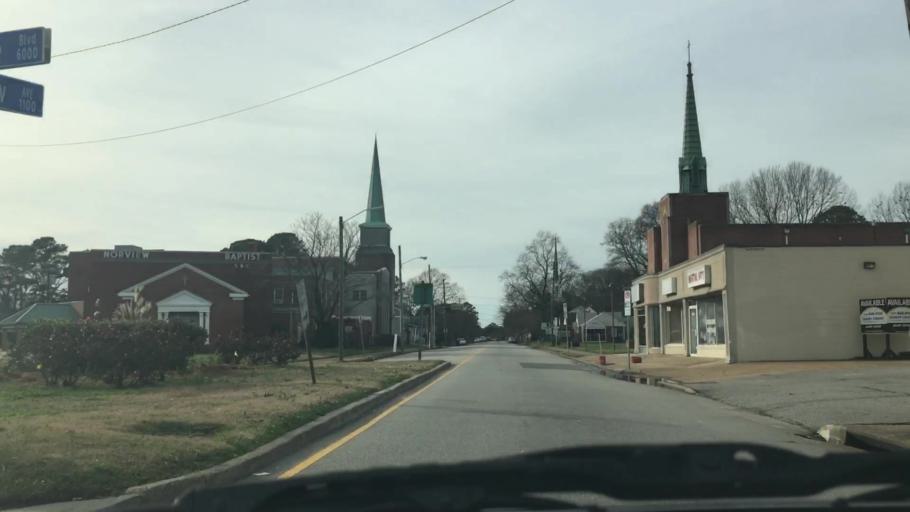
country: US
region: Virginia
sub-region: City of Norfolk
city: Norfolk
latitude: 36.8897
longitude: -76.2390
